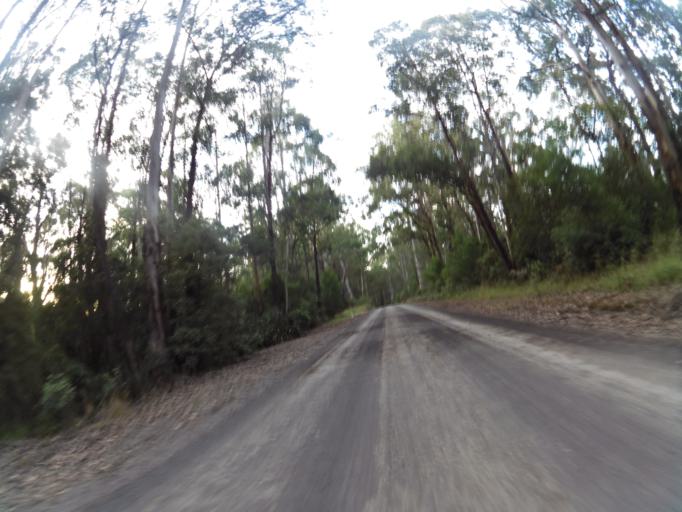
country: AU
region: Victoria
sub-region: Colac-Otway
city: Apollo Bay
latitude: -38.5391
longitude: 143.7297
